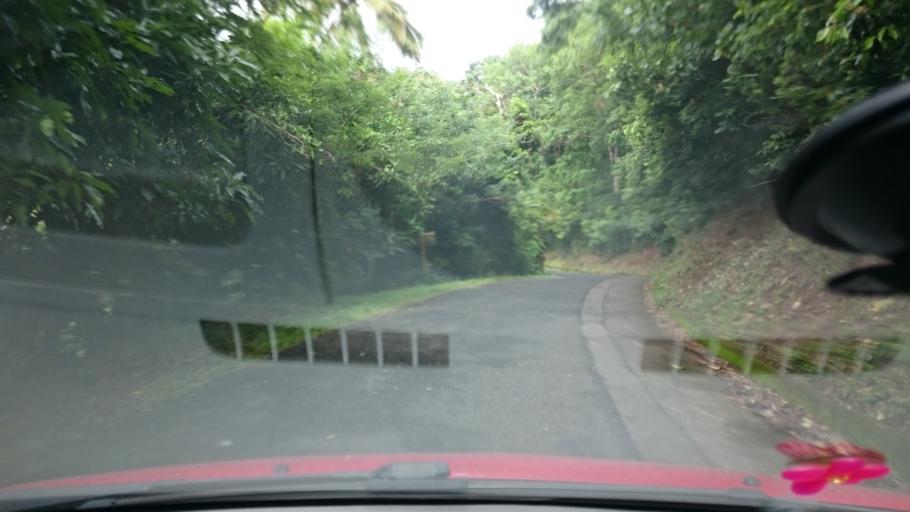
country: MQ
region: Martinique
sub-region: Martinique
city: Riviere-Pilote
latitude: 14.5009
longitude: -60.9193
